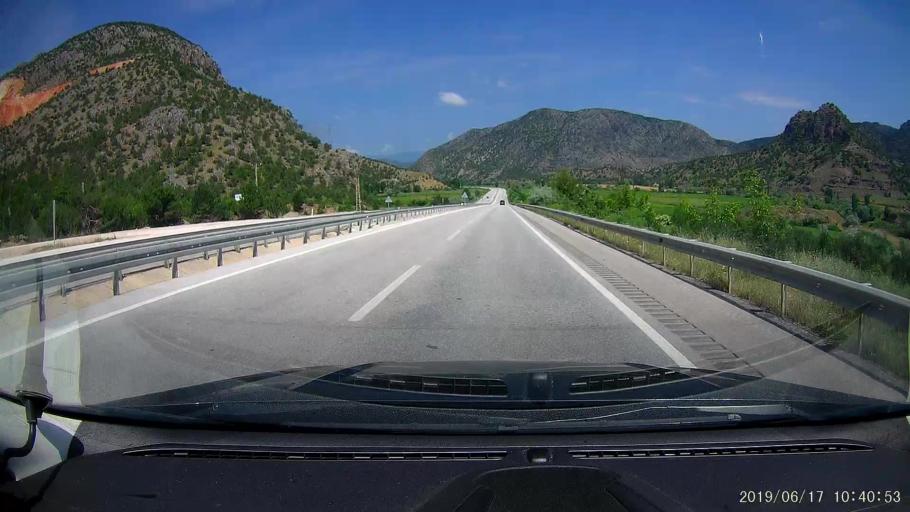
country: TR
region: Corum
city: Kargi
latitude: 41.0310
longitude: 34.5875
